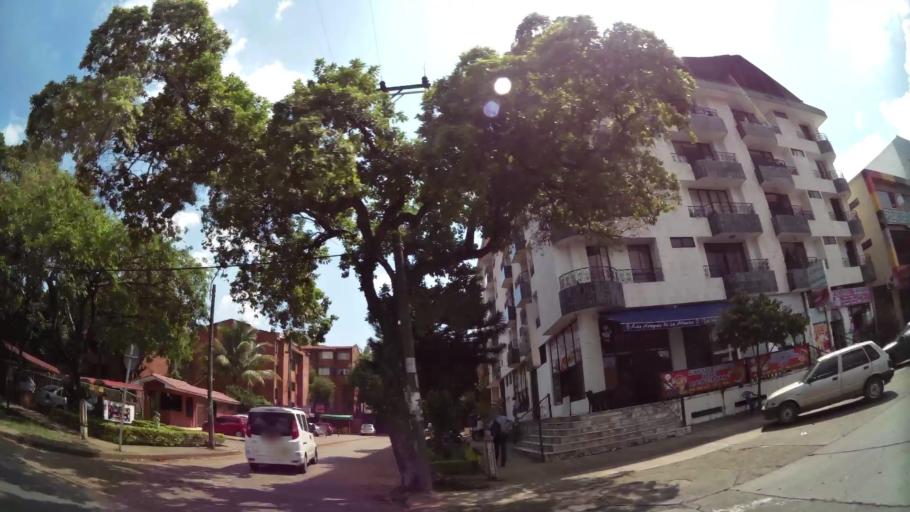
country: CO
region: Valle del Cauca
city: Cali
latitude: 3.4056
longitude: -76.5369
